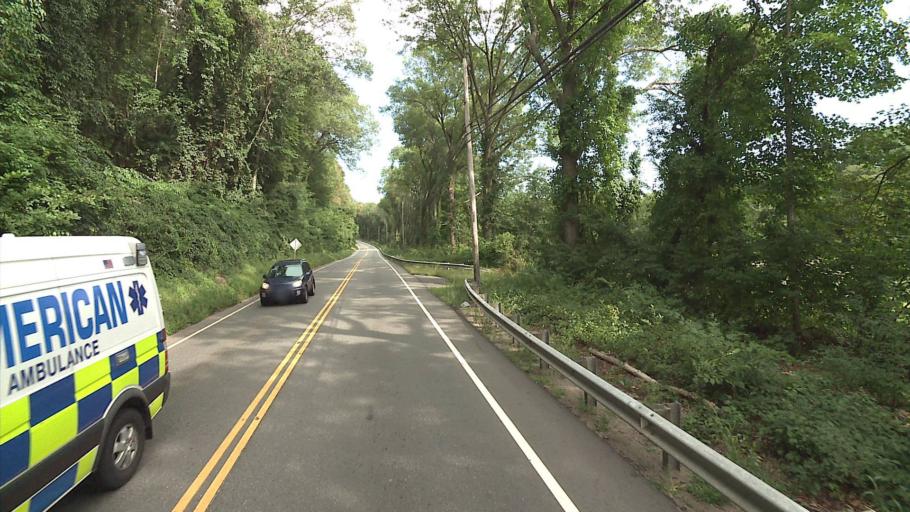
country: US
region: Connecticut
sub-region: New London County
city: Baltic
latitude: 41.5973
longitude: -72.1307
